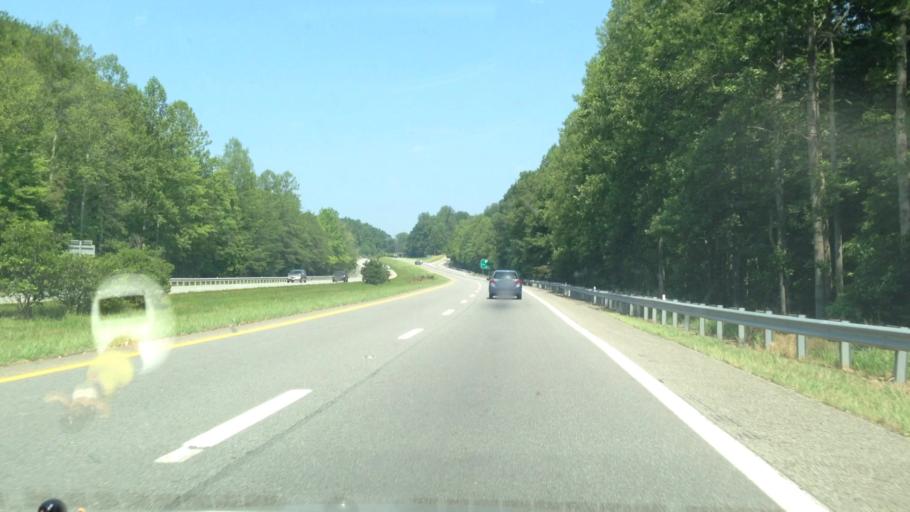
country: US
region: Virginia
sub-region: Henry County
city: Collinsville
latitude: 36.6901
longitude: -79.9447
